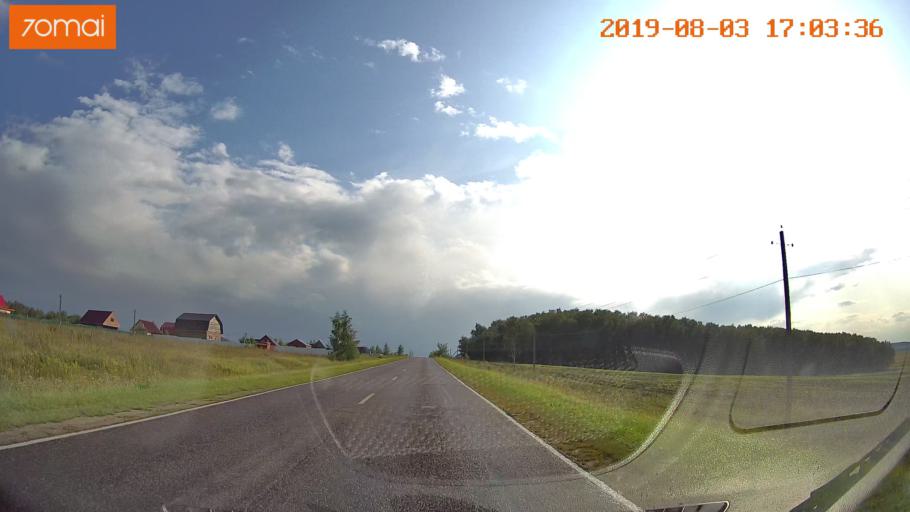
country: RU
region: Moskovskaya
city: Troitskoye
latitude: 55.3358
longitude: 38.5689
